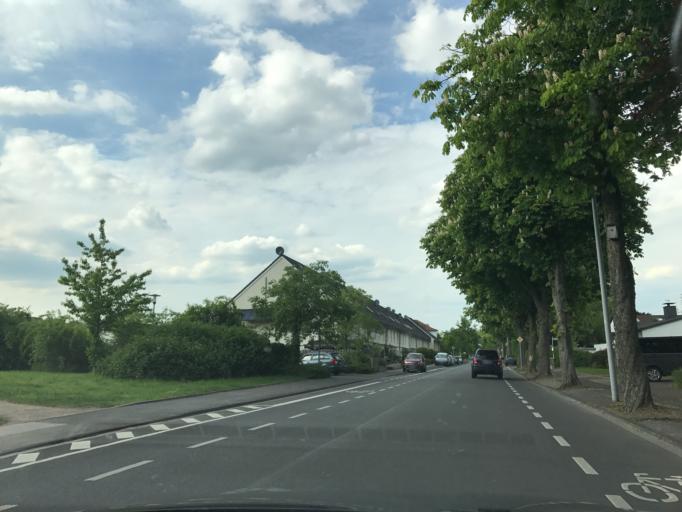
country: DE
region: North Rhine-Westphalia
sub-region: Regierungsbezirk Dusseldorf
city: Muelheim (Ruhr)
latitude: 51.4105
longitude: 6.9062
